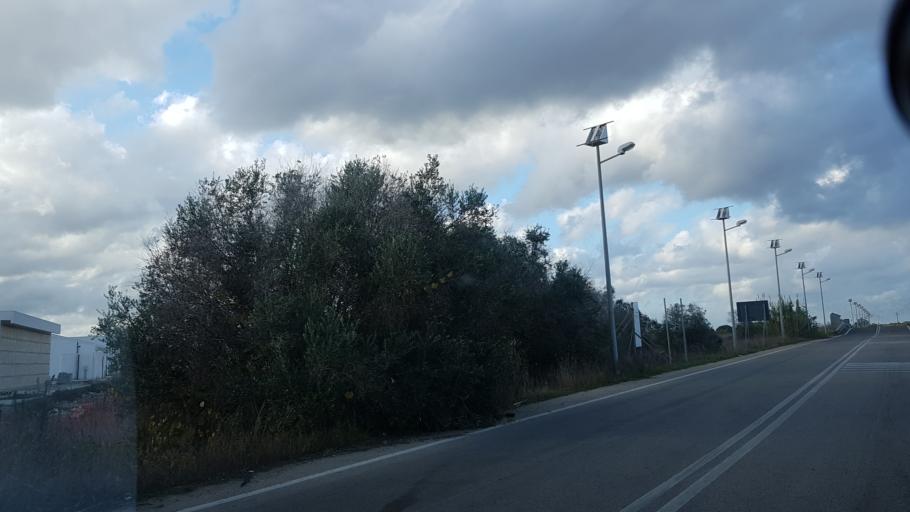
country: IT
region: Apulia
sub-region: Provincia di Brindisi
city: San Pietro Vernotico
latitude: 40.4884
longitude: 18.0106
